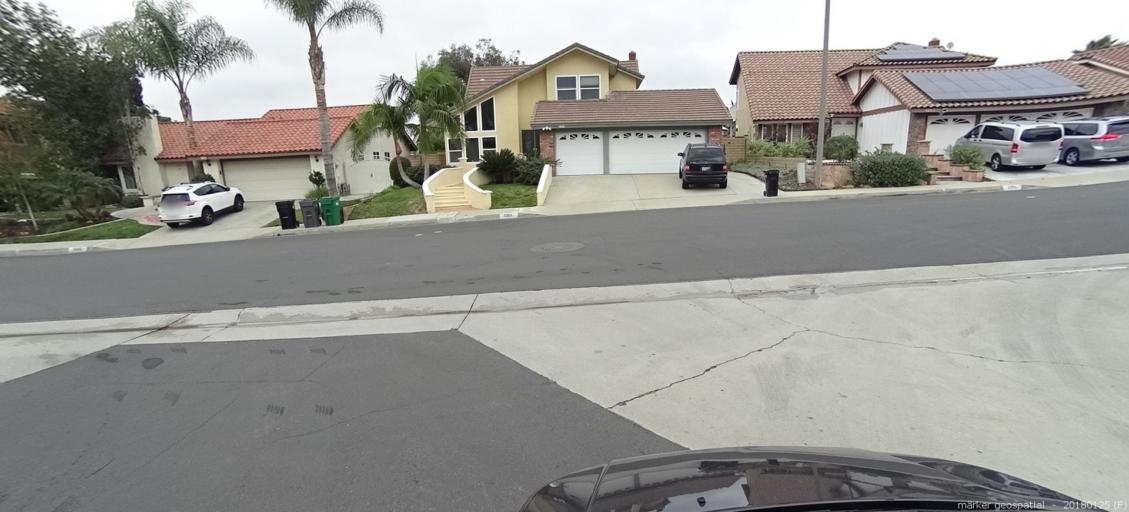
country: US
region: California
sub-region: Los Angeles County
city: Walnut
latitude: 33.9672
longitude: -117.8379
